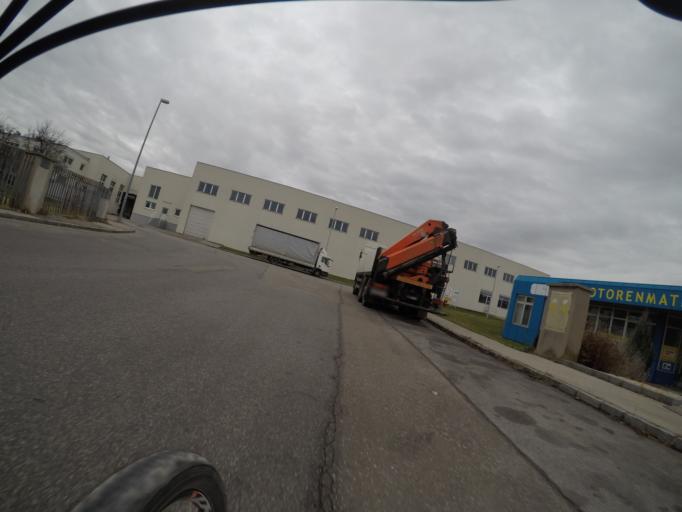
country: AT
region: Lower Austria
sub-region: Politischer Bezirk Modling
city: Brunn am Gebirge
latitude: 48.1099
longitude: 16.3116
